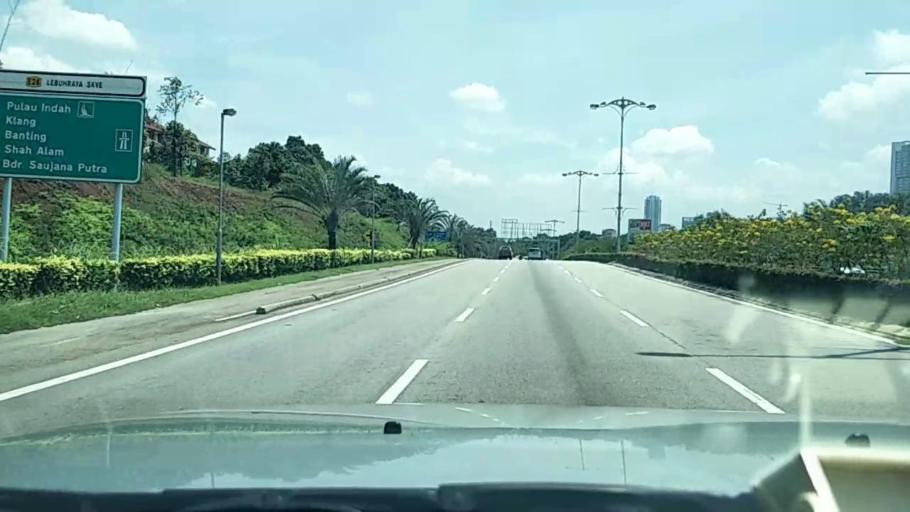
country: MY
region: Putrajaya
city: Putrajaya
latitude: 2.9459
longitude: 101.6729
